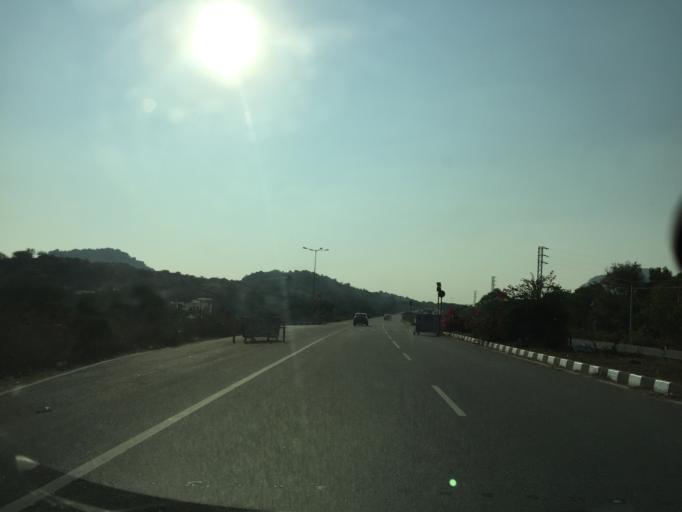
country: IN
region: Telangana
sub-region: Nalgonda
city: Bhongir
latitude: 17.5150
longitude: 78.9141
